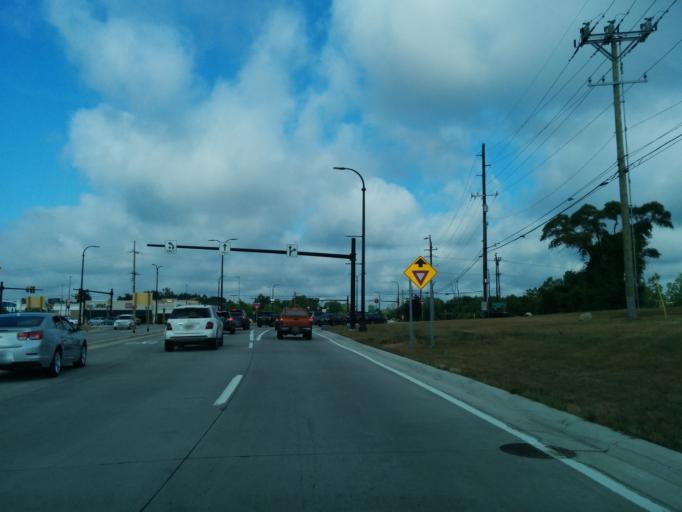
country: US
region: Michigan
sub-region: Oakland County
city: Farmington Hills
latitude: 42.5285
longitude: -83.3588
